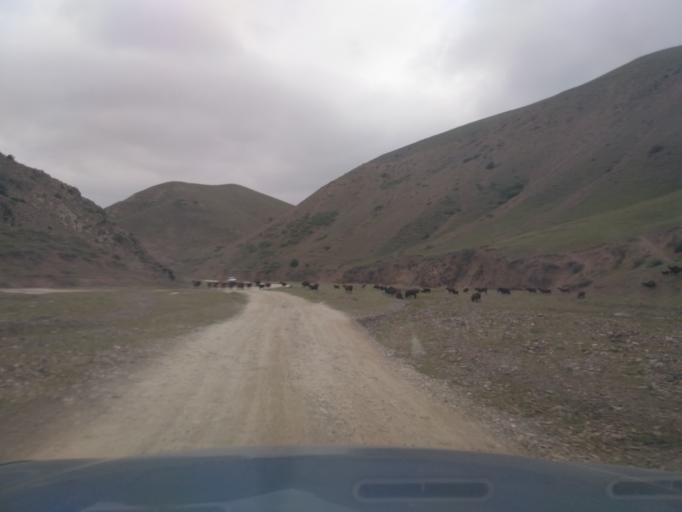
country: UZ
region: Jizzax
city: Zomin
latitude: 39.8495
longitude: 68.3963
